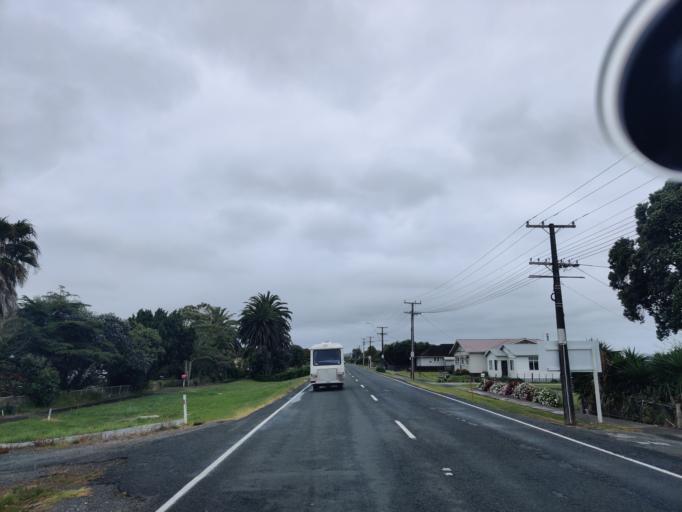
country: NZ
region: Northland
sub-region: Kaipara District
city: Dargaville
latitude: -36.1349
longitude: 174.0261
